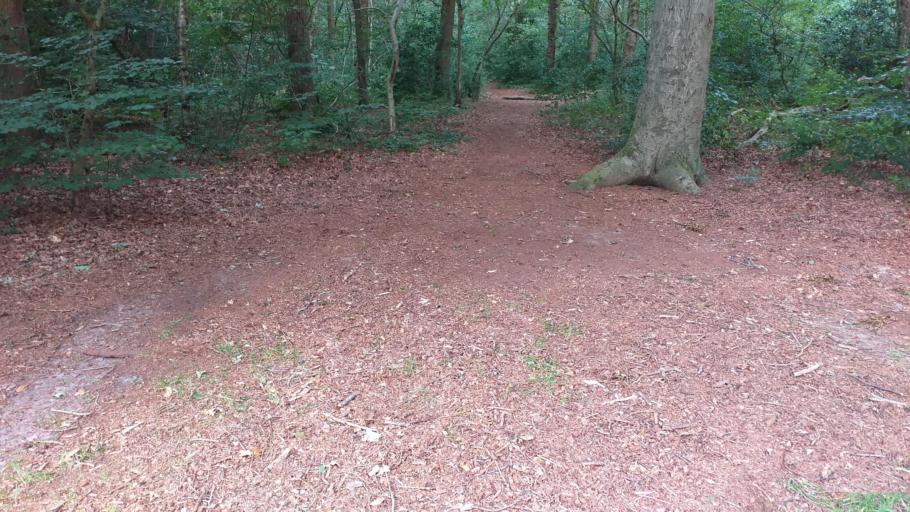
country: NL
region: North Holland
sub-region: Gemeente Heiloo
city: Heiloo
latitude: 52.6745
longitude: 4.6903
